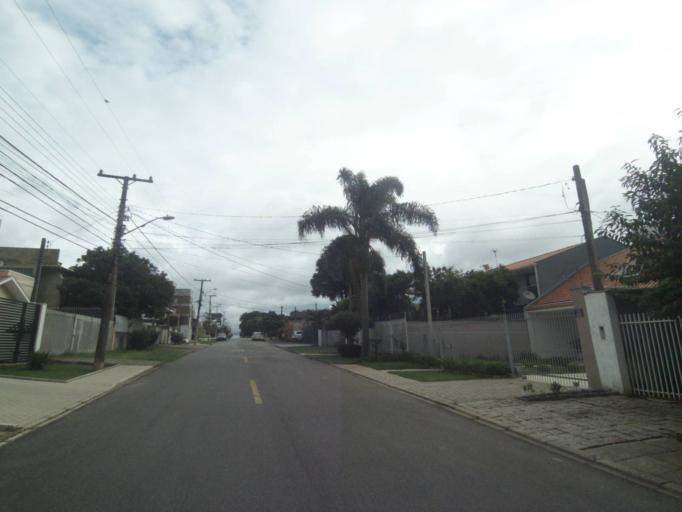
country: BR
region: Parana
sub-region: Curitiba
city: Curitiba
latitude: -25.4947
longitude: -49.3065
